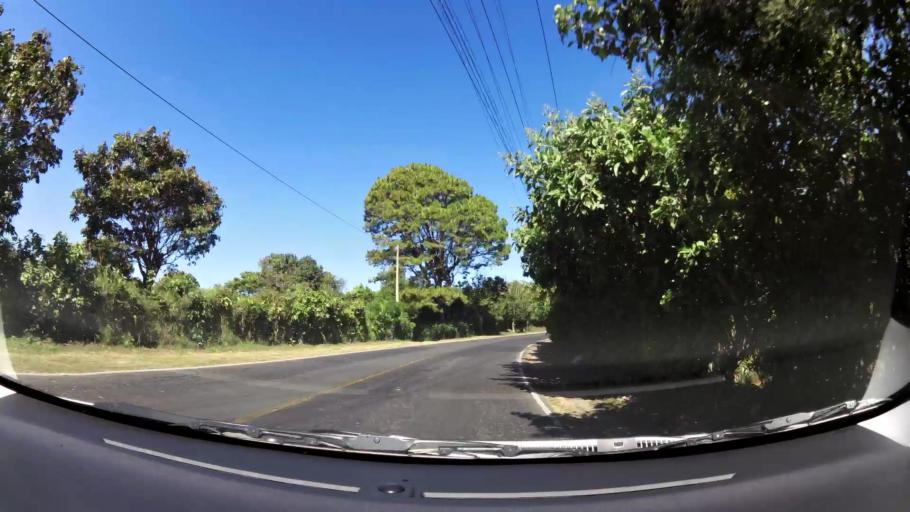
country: SV
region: Ahuachapan
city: Concepcion de Ataco
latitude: 13.8579
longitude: -89.8501
